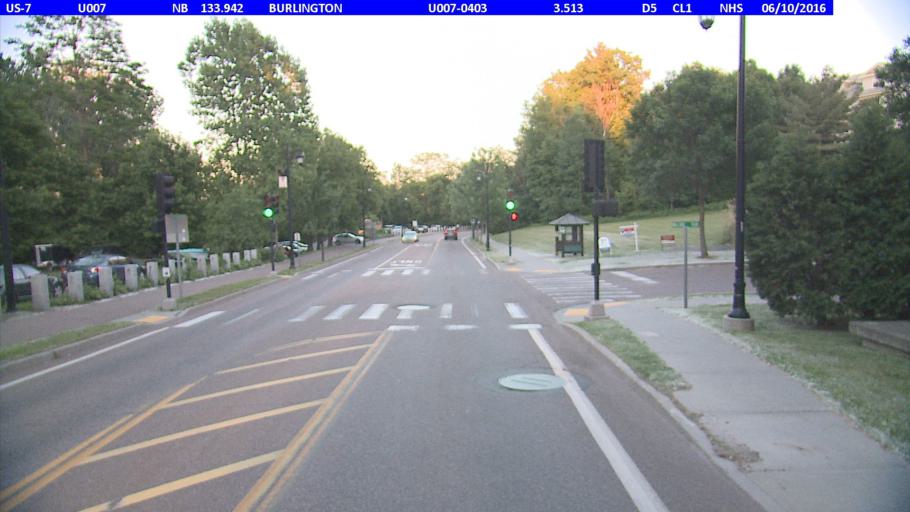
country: US
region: Vermont
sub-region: Chittenden County
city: Winooski
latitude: 44.4879
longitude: -73.1967
